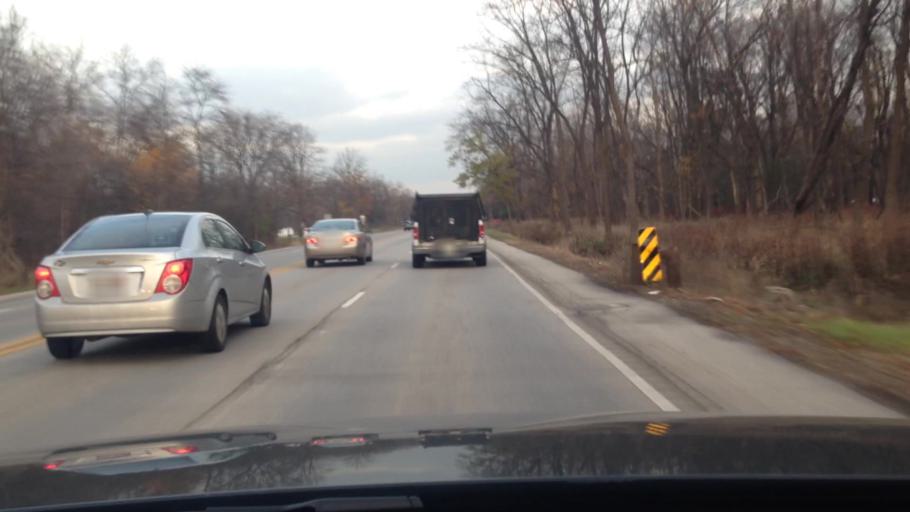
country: US
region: Illinois
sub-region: Cook County
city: Norridge
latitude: 41.9526
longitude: -87.8478
